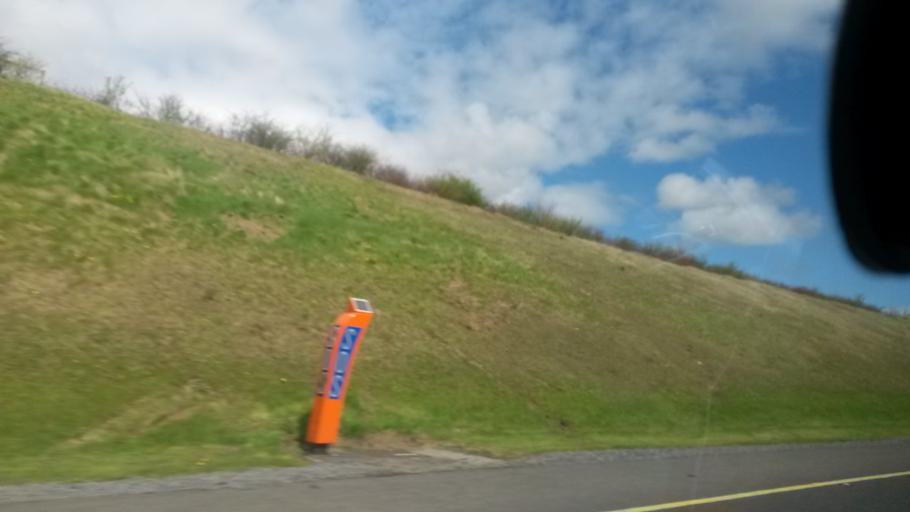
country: IE
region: Leinster
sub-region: Kildare
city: Kildare
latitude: 53.1560
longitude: -6.8695
